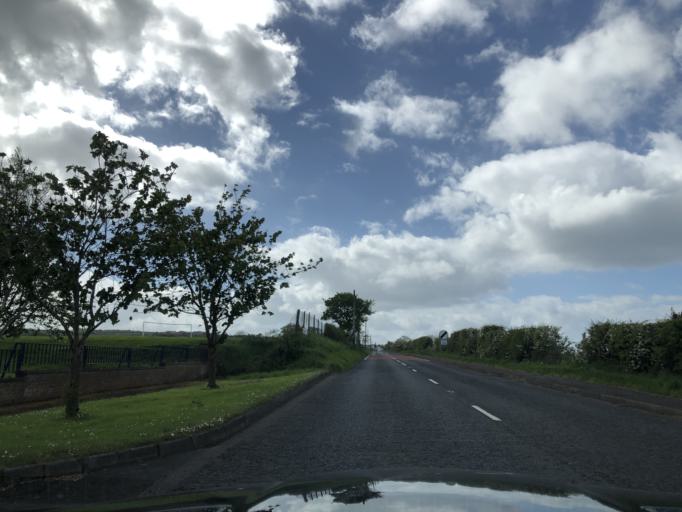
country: GB
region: Northern Ireland
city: Bushmills
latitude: 55.2063
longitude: -6.5315
